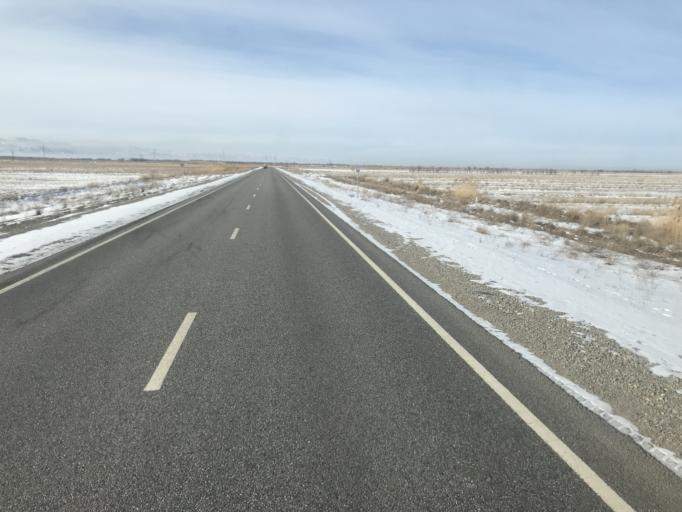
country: KZ
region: Zhambyl
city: Taraz
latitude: 43.0074
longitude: 71.2741
